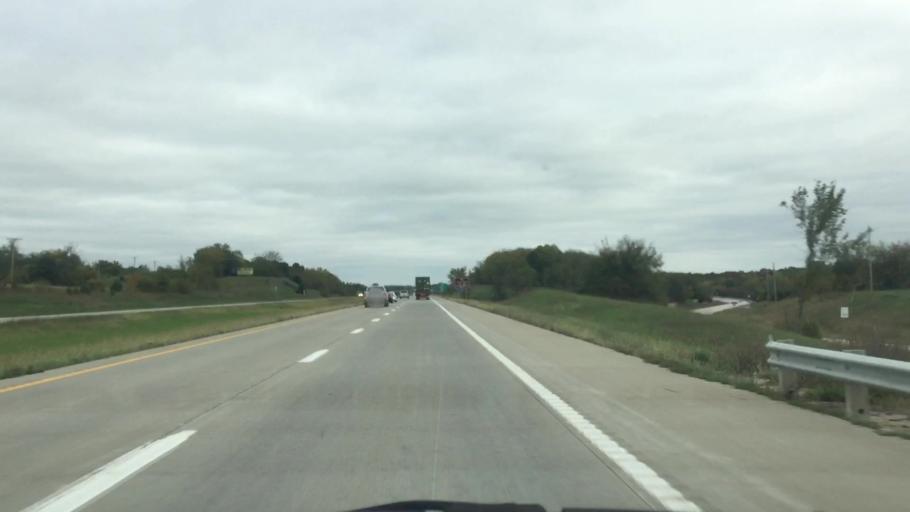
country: US
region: Missouri
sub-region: Clinton County
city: Cameron
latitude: 39.6595
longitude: -94.2377
